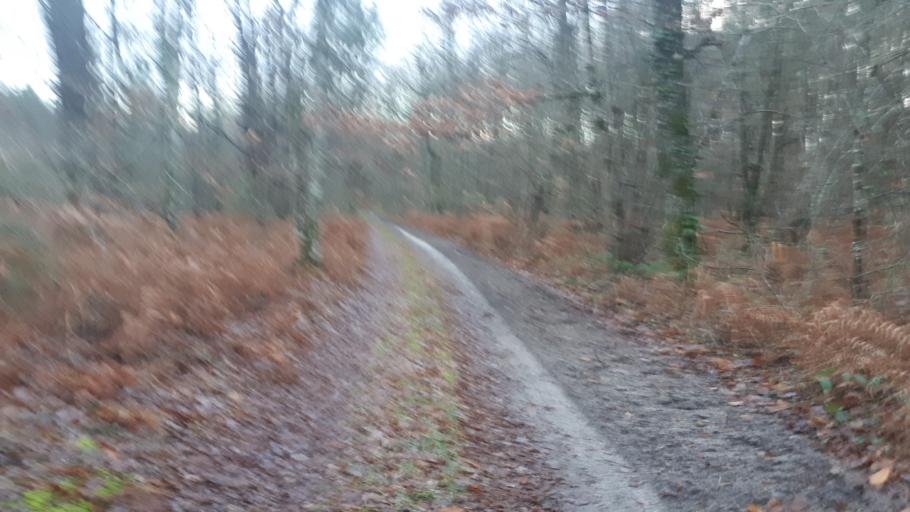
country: FR
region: Centre
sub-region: Departement du Loir-et-Cher
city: Saint-Romain-sur-Cher
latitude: 47.3420
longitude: 1.3961
